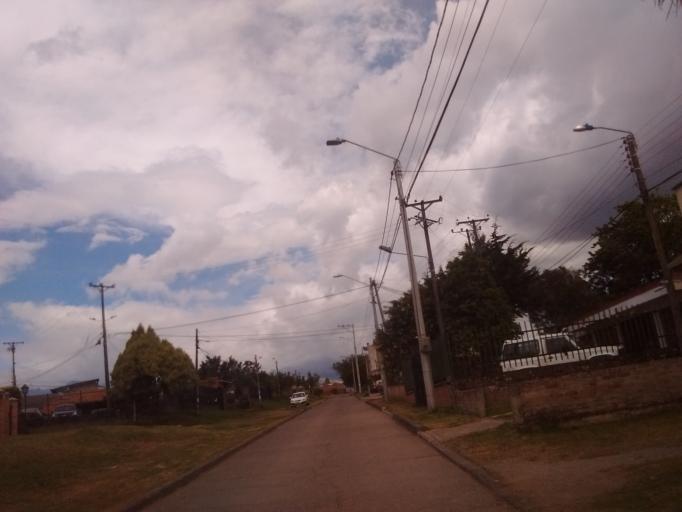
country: CO
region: Cauca
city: Popayan
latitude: 2.4921
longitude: -76.5637
